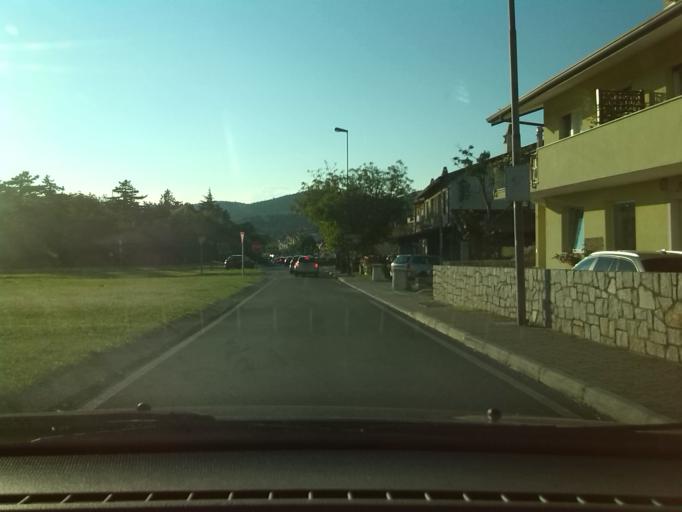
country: IT
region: Friuli Venezia Giulia
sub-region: Provincia di Trieste
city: Sistiana-Visogliano
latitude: 45.7700
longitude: 13.6397
